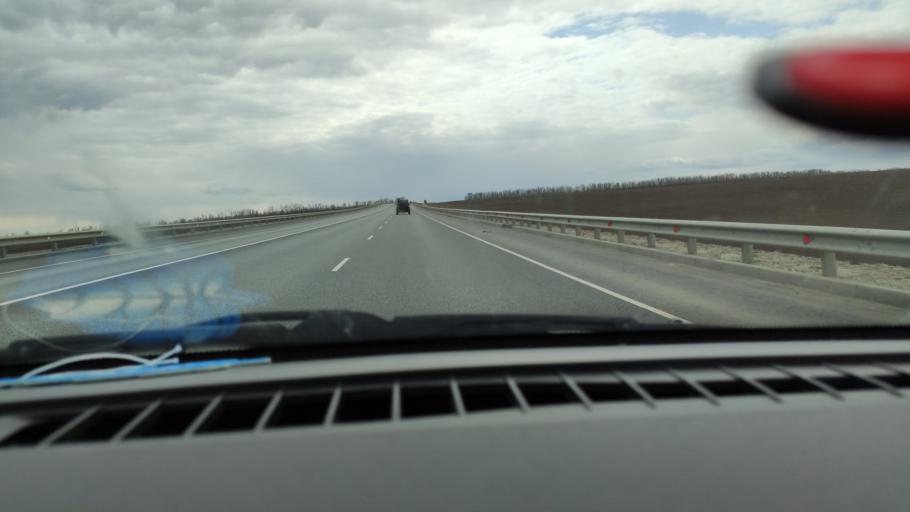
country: RU
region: Saratov
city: Yelshanka
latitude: 51.8365
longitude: 46.4722
